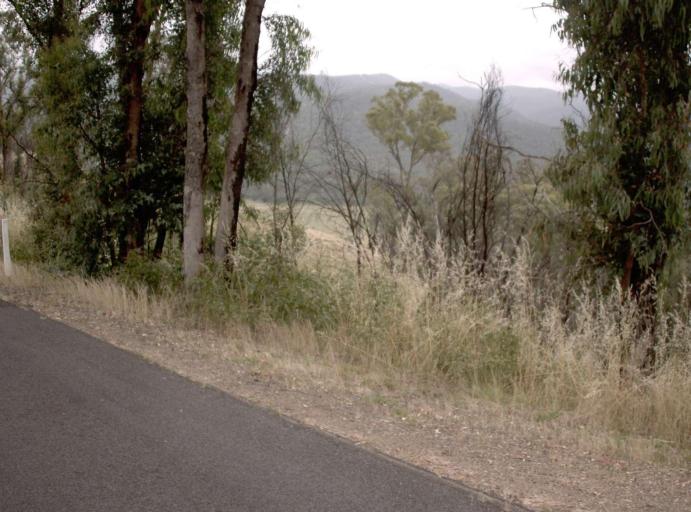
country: AU
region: Victoria
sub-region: Wellington
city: Heyfield
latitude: -37.8235
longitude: 146.6754
